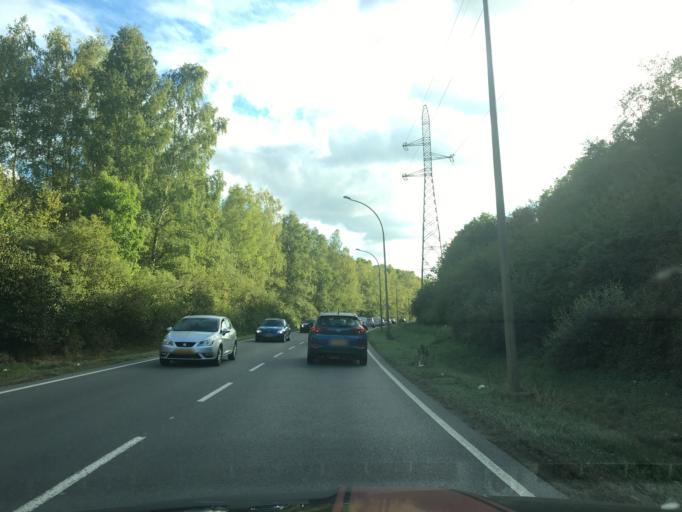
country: LU
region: Luxembourg
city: Soleuvre
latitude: 49.5301
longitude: 5.9275
